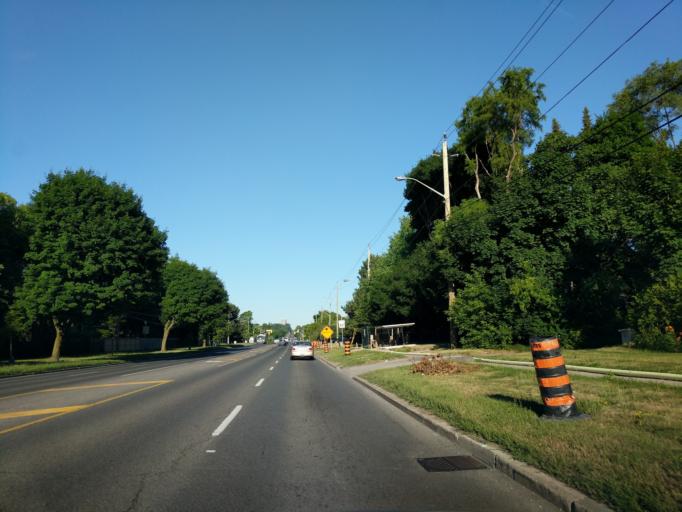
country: CA
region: Ontario
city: Willowdale
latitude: 43.8048
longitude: -79.3899
